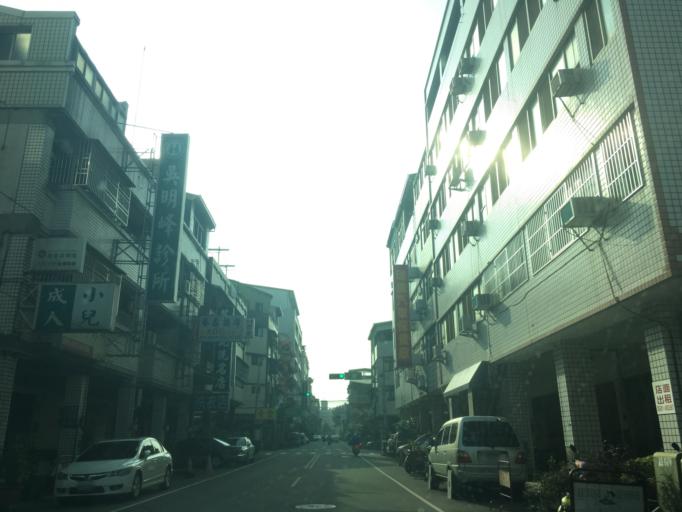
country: TW
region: Taiwan
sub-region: Taichung City
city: Taichung
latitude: 24.1683
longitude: 120.6856
